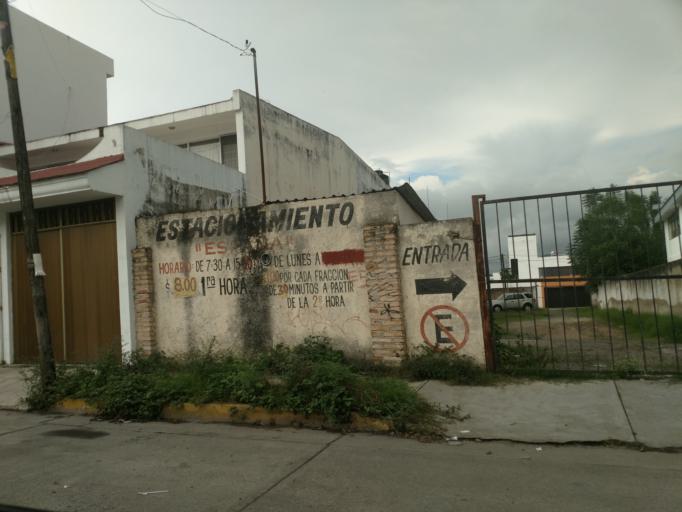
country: MX
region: Nayarit
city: Tepic
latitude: 21.4867
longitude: -104.8818
